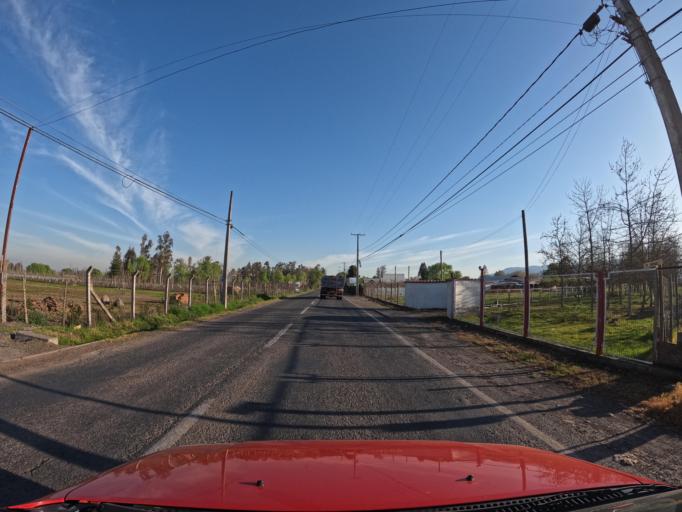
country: CL
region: Maule
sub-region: Provincia de Curico
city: Rauco
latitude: -34.8792
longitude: -71.2693
